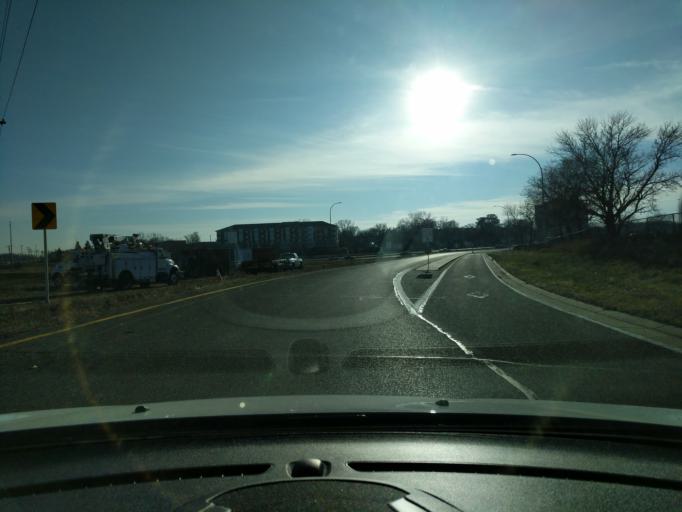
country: US
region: Minnesota
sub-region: Ramsey County
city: Roseville
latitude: 45.0120
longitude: -93.1671
